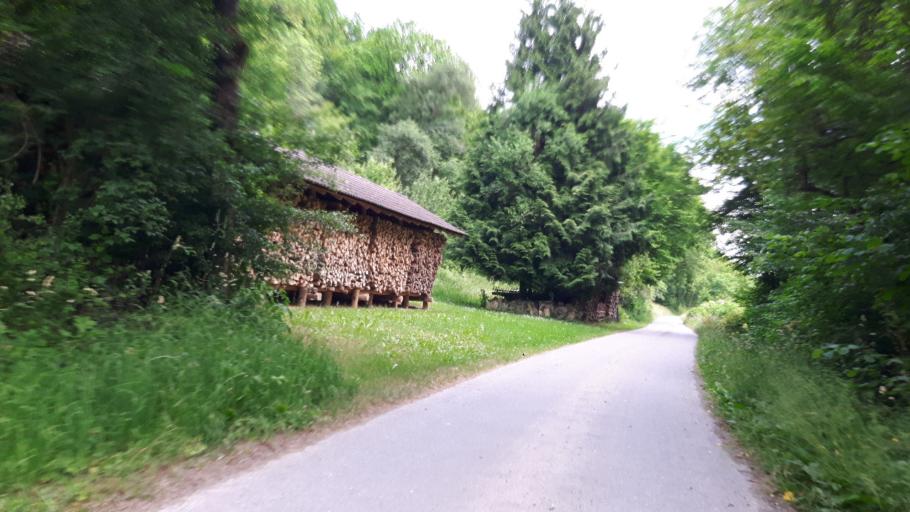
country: DE
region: Baden-Wuerttemberg
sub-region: Regierungsbezirk Stuttgart
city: Jagsthausen
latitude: 49.2845
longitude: 9.4685
